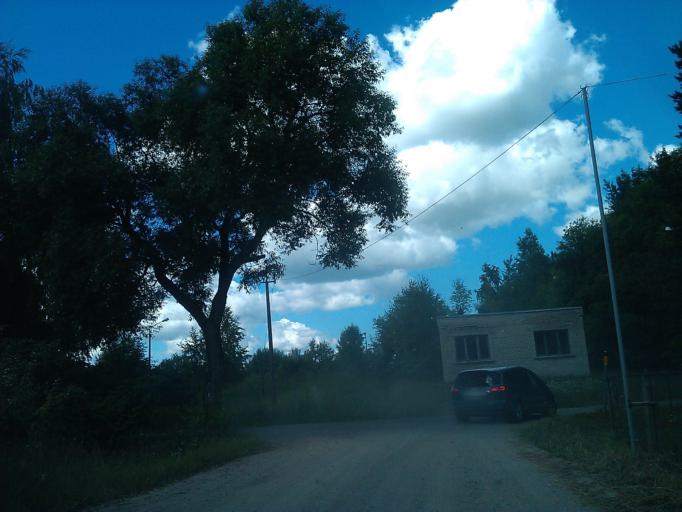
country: LV
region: Vilanu
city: Vilani
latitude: 56.5904
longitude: 26.9501
